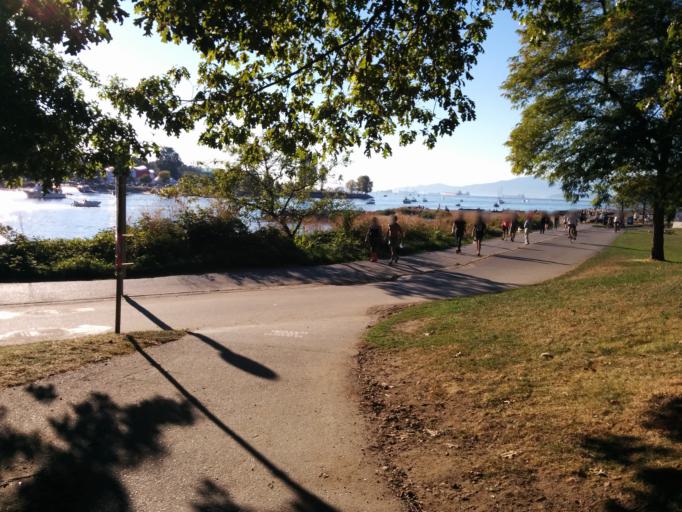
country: CA
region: British Columbia
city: West End
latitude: 49.2773
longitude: -123.1360
